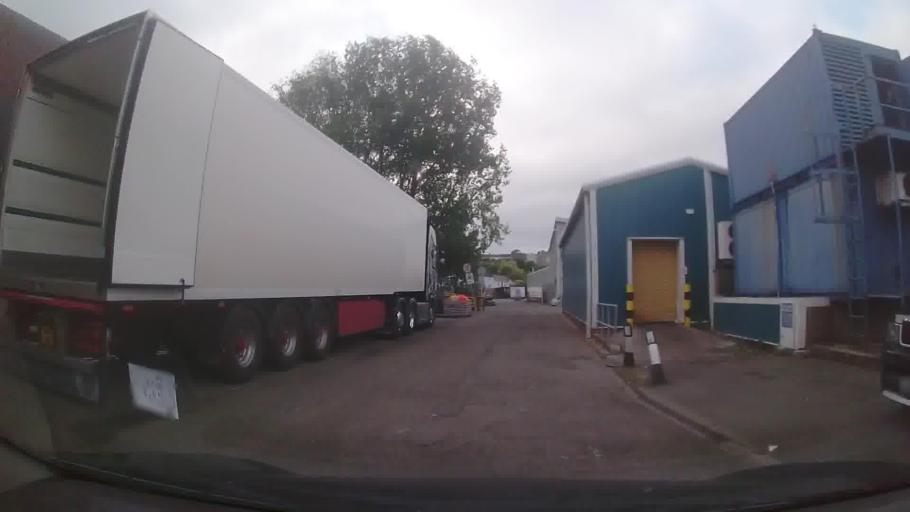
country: GB
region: Wales
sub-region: Pembrokeshire
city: Milford Haven
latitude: 51.7108
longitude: -5.0412
